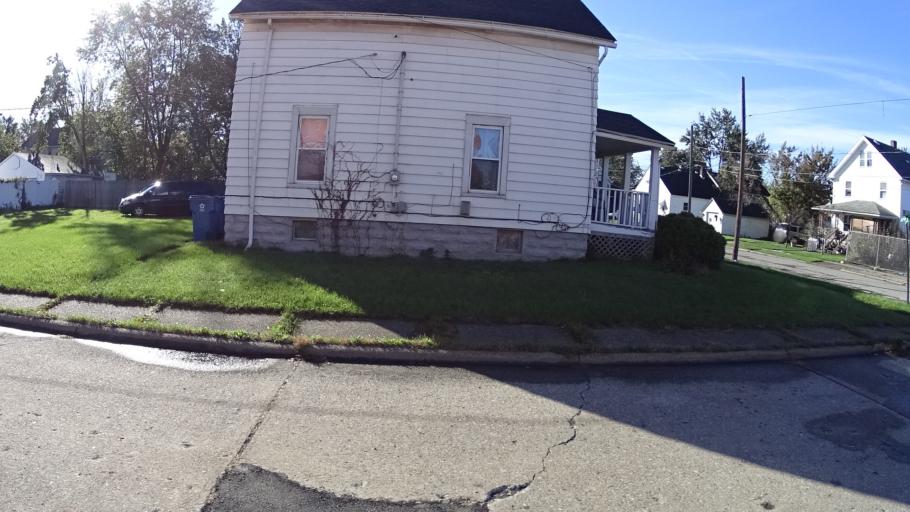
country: US
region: Ohio
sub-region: Lorain County
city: Lorain
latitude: 41.4442
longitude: -82.1632
